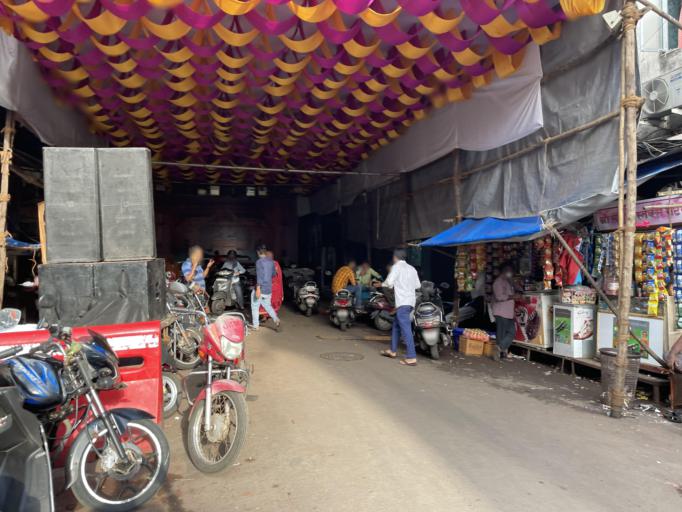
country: IN
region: Maharashtra
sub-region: Mumbai Suburban
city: Mumbai
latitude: 18.9603
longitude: 72.8277
